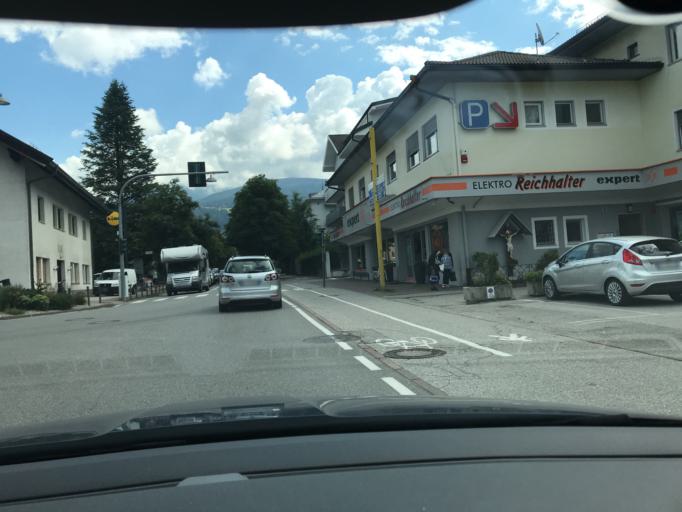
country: IT
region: Trentino-Alto Adige
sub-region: Bolzano
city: Brunico
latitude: 46.7933
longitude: 11.9316
